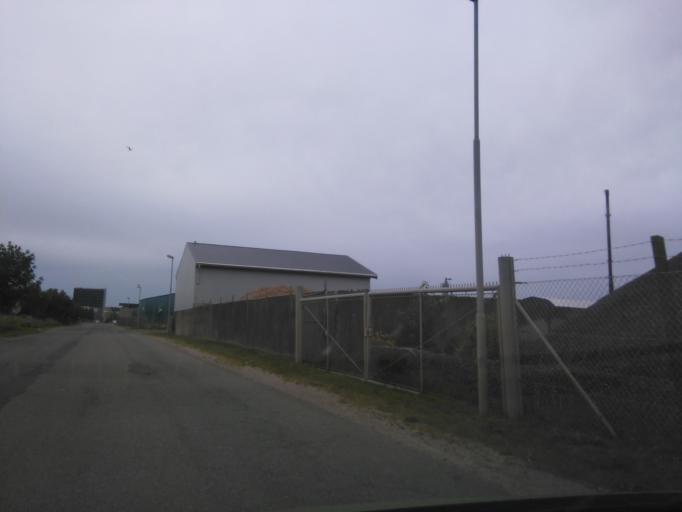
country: DK
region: Central Jutland
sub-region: Horsens Kommune
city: Horsens
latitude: 55.8552
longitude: 9.8600
